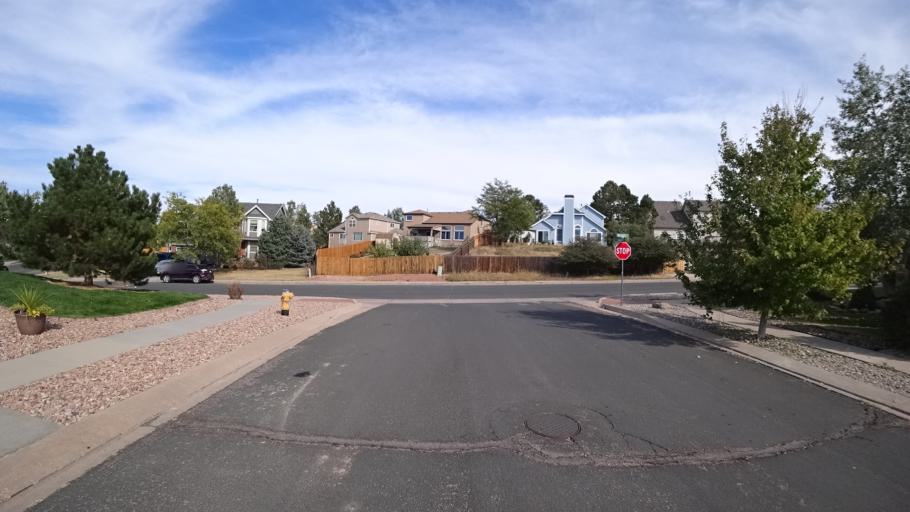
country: US
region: Colorado
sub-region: El Paso County
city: Cimarron Hills
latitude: 38.9040
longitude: -104.6947
